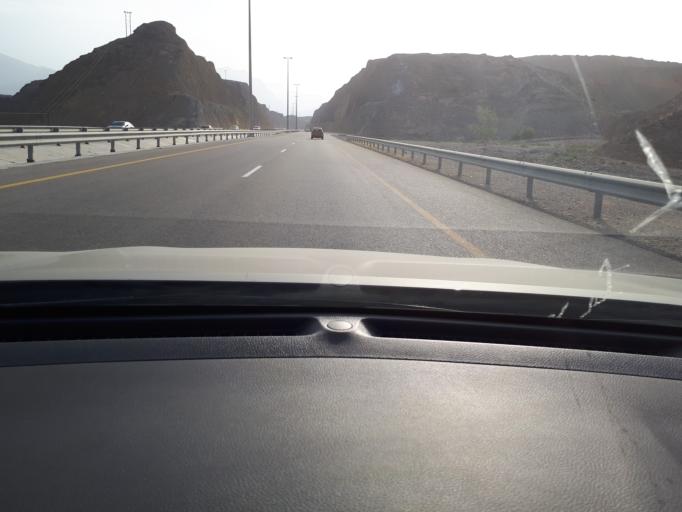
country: OM
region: Muhafazat Masqat
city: Muscat
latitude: 23.1907
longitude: 58.8718
